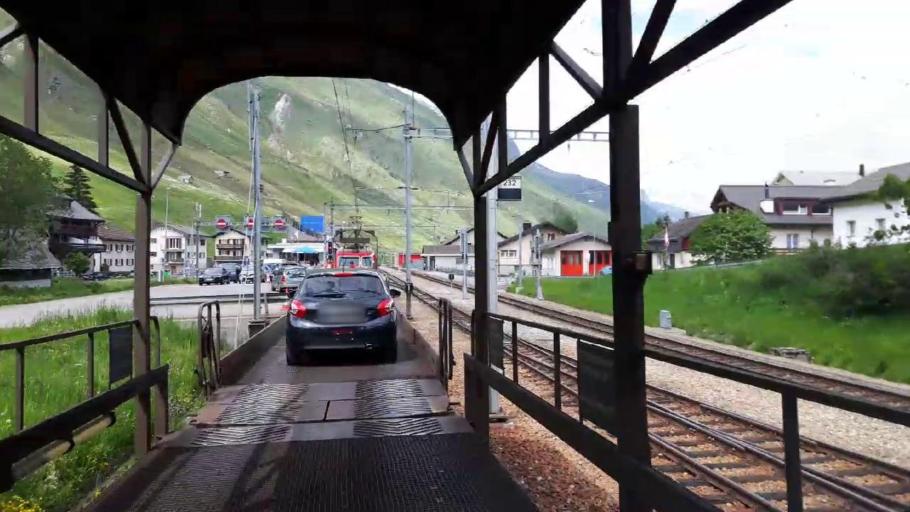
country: CH
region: Uri
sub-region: Uri
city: Andermatt
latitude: 46.5974
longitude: 8.5024
